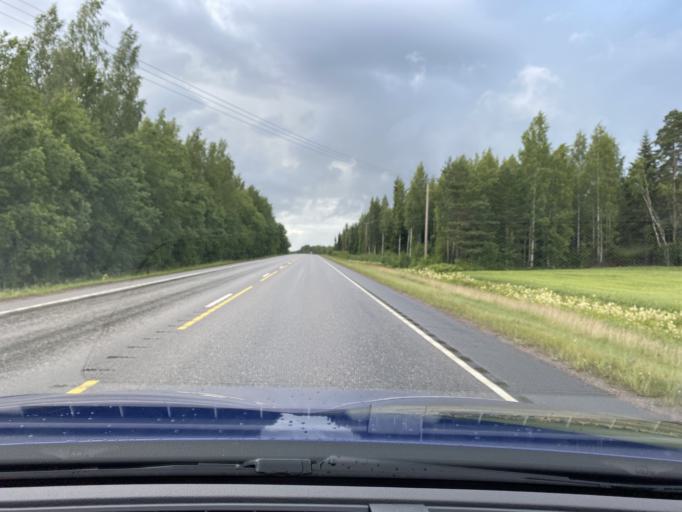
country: FI
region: Uusimaa
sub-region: Helsinki
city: Hyvinge
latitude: 60.5534
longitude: 24.8245
